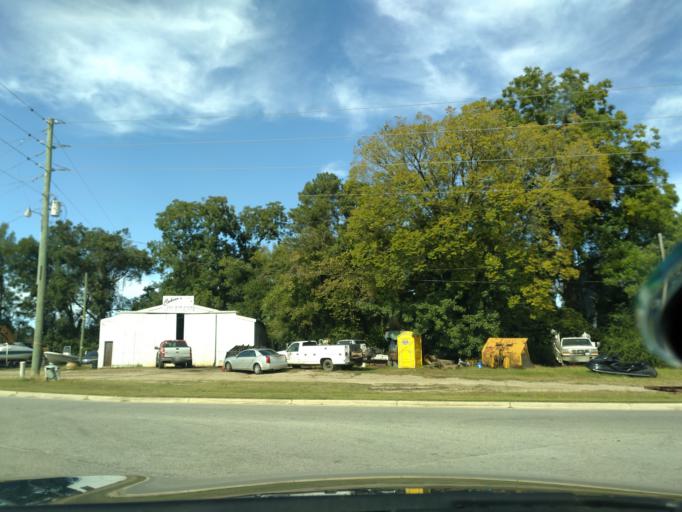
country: US
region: North Carolina
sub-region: Beaufort County
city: Belhaven
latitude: 35.5890
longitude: -76.6623
